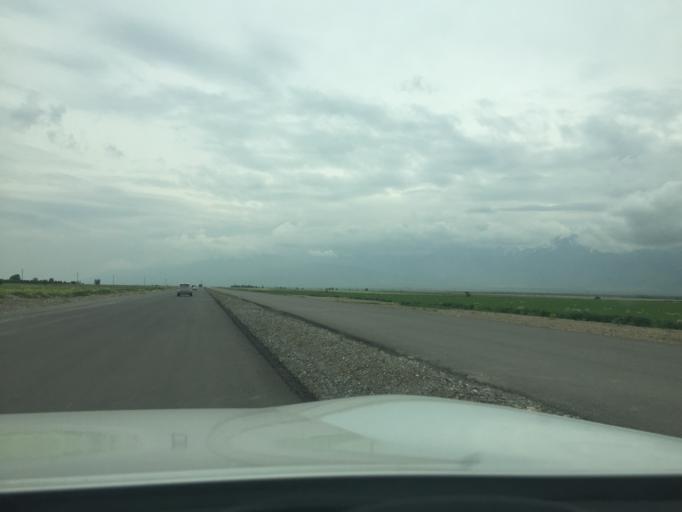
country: KZ
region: Ongtustik Qazaqstan
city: Turar Ryskulov
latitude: 42.5116
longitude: 70.3872
